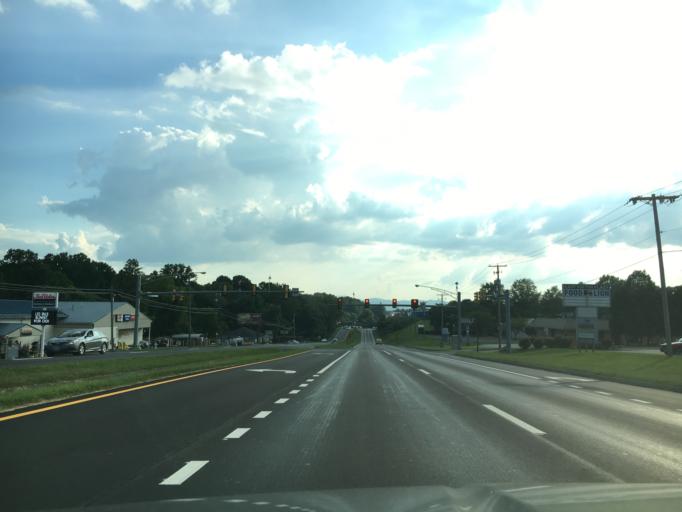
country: US
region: Virginia
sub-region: Roanoke County
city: Vinton
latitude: 37.2798
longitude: -79.8648
